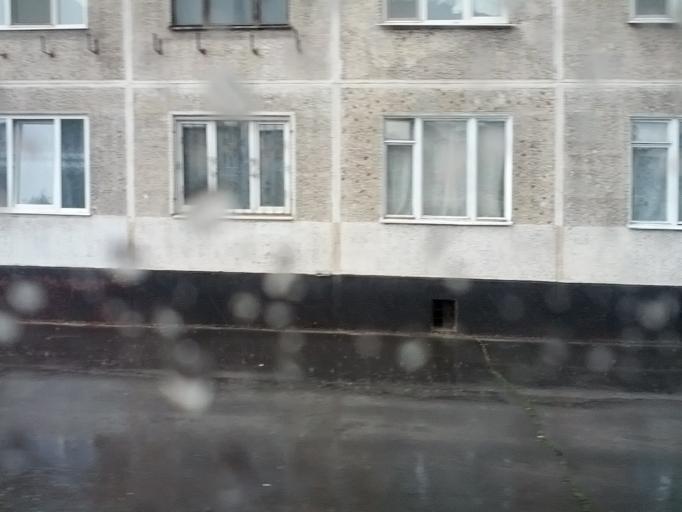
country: RU
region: St.-Petersburg
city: Obukhovo
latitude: 59.8837
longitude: 30.4687
